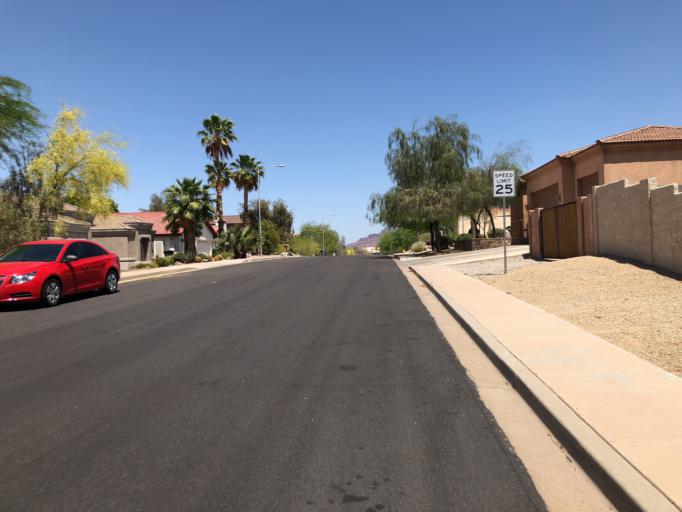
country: US
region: Arizona
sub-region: Maricopa County
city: Mesa
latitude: 33.4672
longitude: -111.6953
